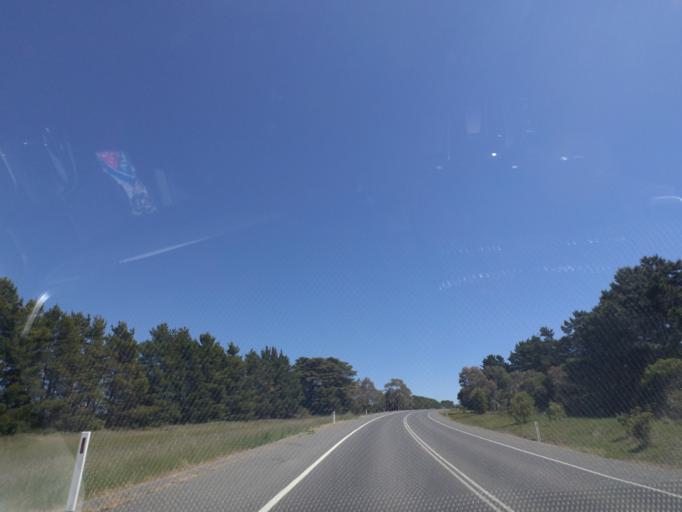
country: AU
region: Victoria
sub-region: Hume
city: Sunbury
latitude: -37.3106
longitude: 144.8461
